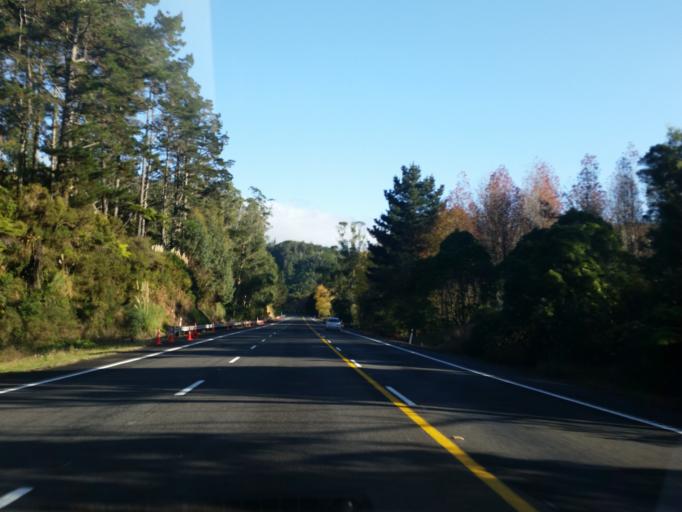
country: NZ
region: Bay of Plenty
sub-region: Western Bay of Plenty District
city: Waihi Beach
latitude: -37.4580
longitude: 175.9059
